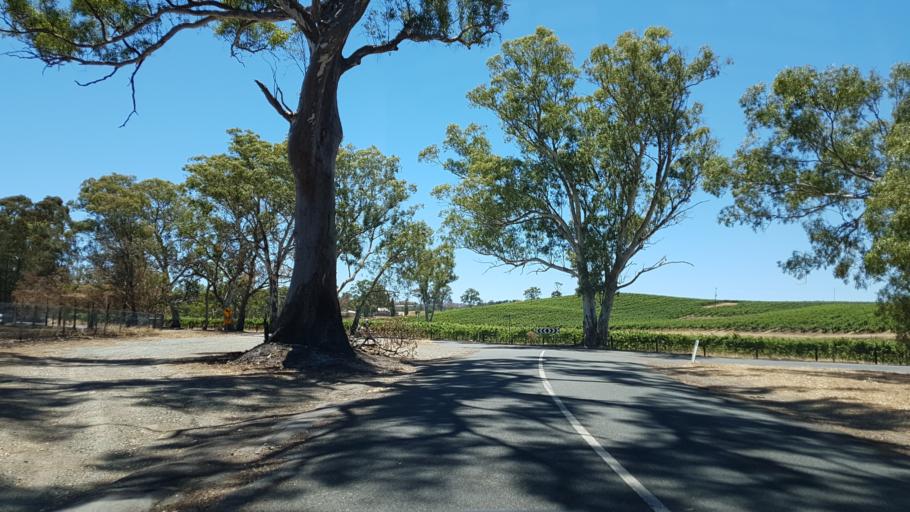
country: AU
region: South Australia
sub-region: Adelaide Hills
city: Lobethal
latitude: -34.8938
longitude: 138.9040
